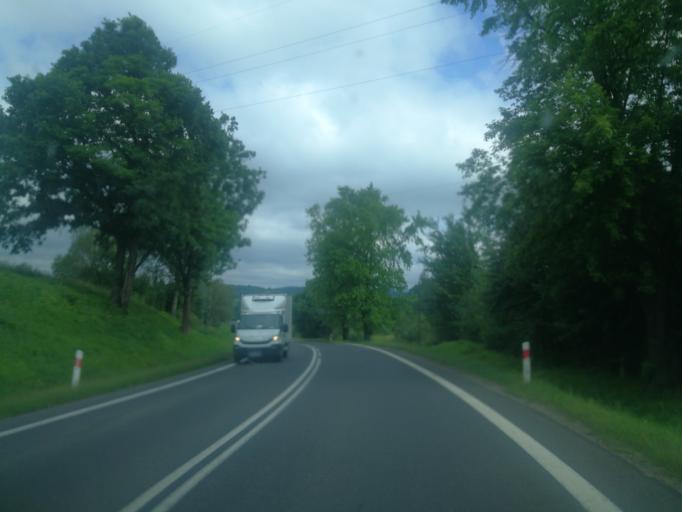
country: PL
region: Subcarpathian Voivodeship
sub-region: Powiat leski
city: Lesko
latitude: 49.4867
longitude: 22.3233
